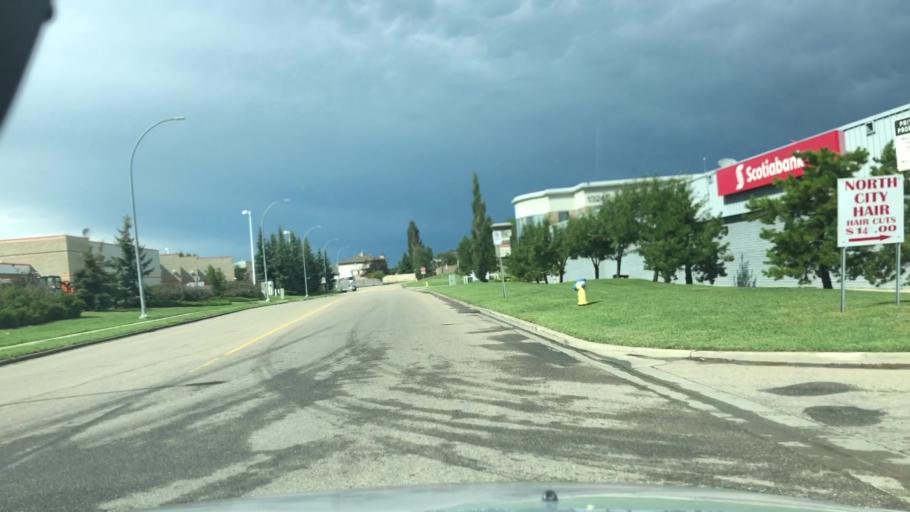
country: CA
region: Alberta
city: St. Albert
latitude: 53.6005
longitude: -113.5506
